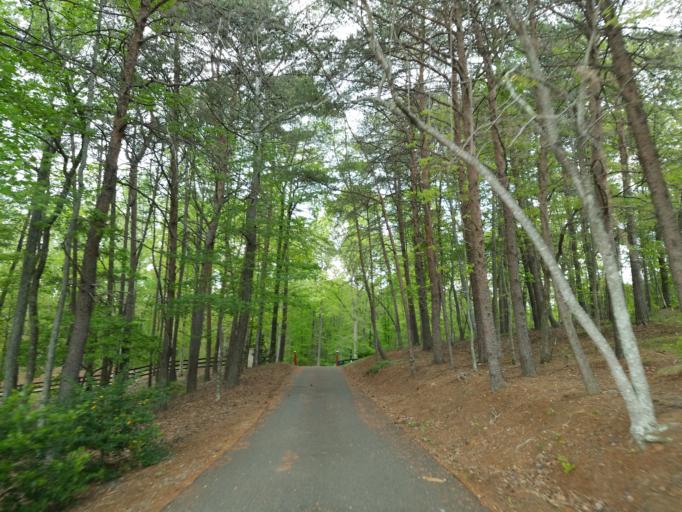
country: US
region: Georgia
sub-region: Pickens County
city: Jasper
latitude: 34.4407
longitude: -84.4876
